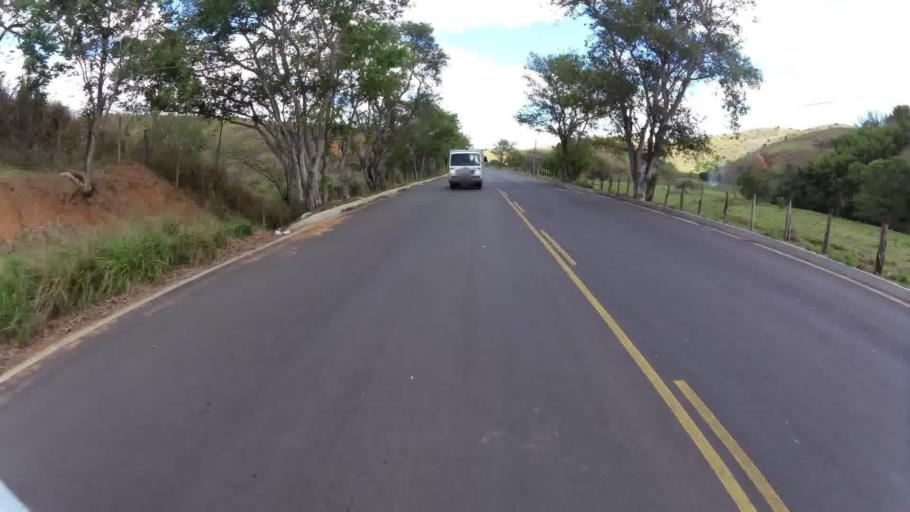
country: BR
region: Rio de Janeiro
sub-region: Cambuci
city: Cambuci
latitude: -21.3886
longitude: -41.9676
